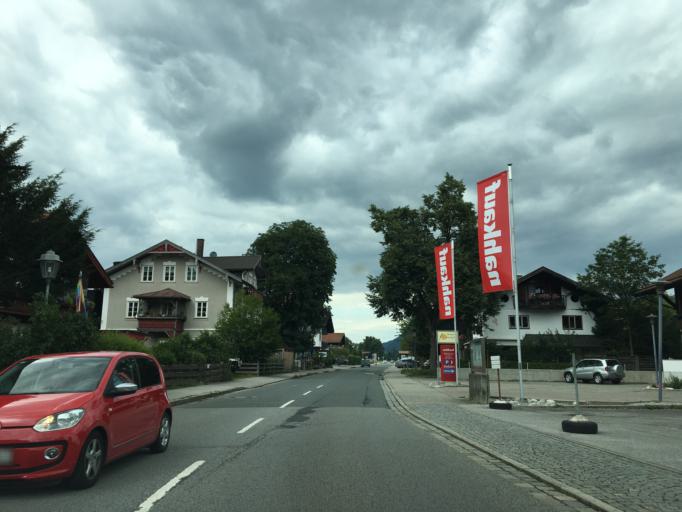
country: DE
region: Bavaria
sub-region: Upper Bavaria
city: Oberaudorf
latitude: 47.6498
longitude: 12.1730
